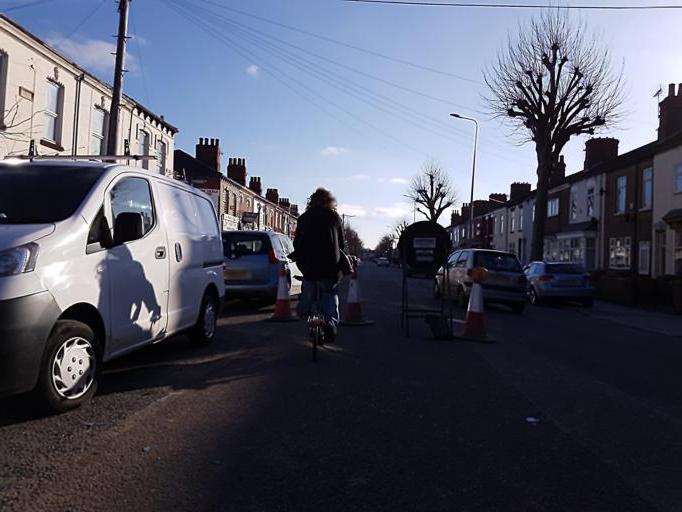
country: GB
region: England
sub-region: North East Lincolnshire
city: Grimsby
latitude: 53.5634
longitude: -0.0758
